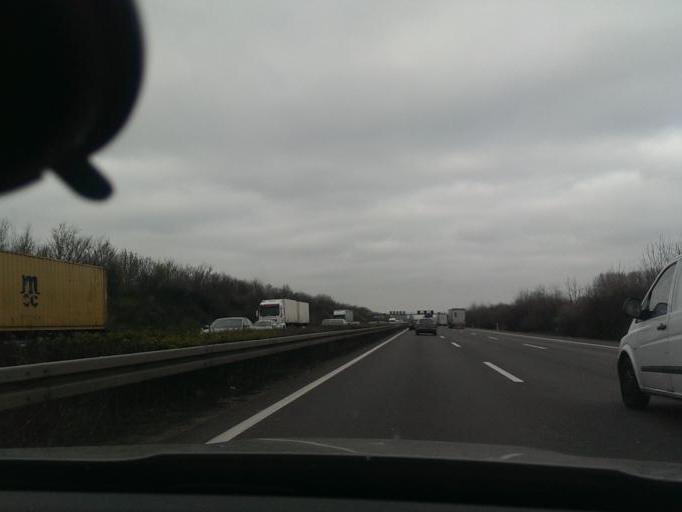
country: DE
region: Lower Saxony
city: Gross Munzel
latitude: 52.3757
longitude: 9.4569
